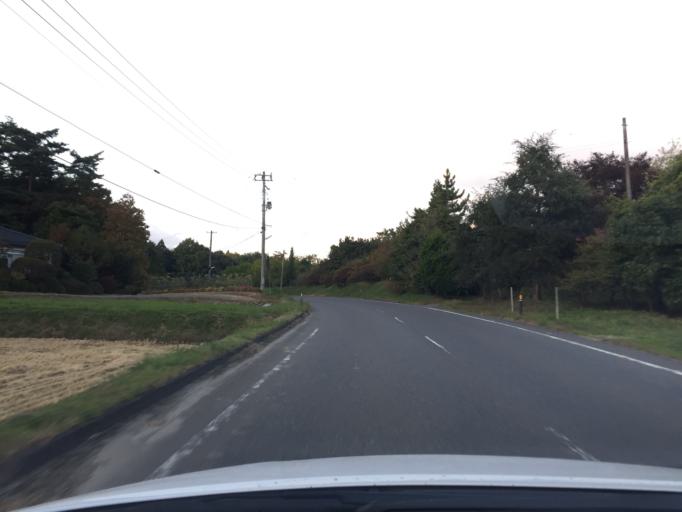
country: JP
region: Fukushima
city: Koriyama
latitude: 37.3552
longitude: 140.4473
